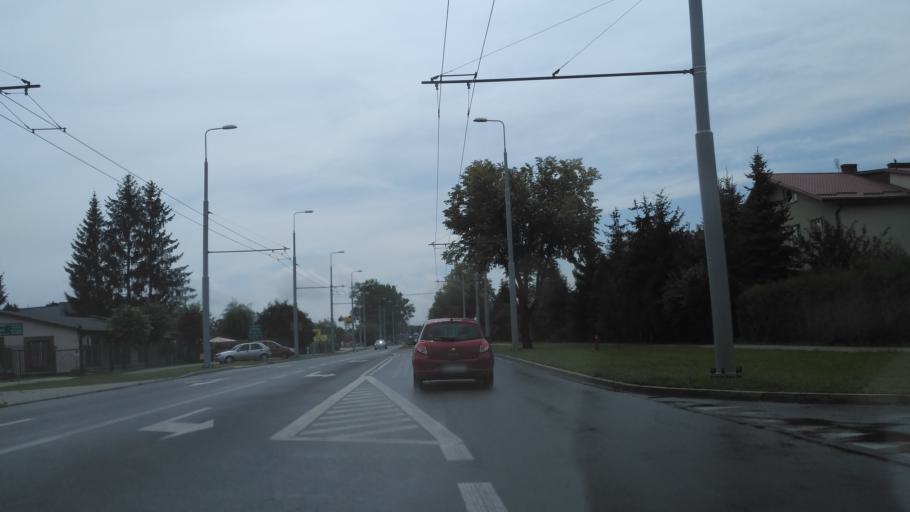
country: PL
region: Lublin Voivodeship
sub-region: Powiat lubelski
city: Lublin
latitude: 51.2027
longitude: 22.5859
